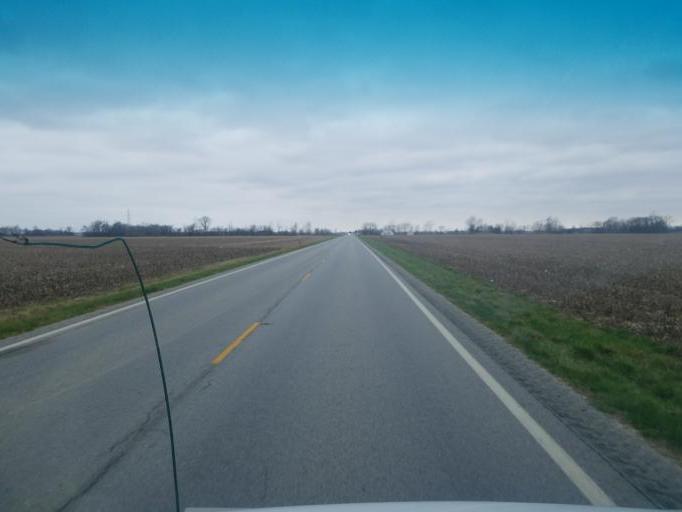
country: US
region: Ohio
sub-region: Allen County
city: Delphos
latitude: 40.9320
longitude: -84.4383
